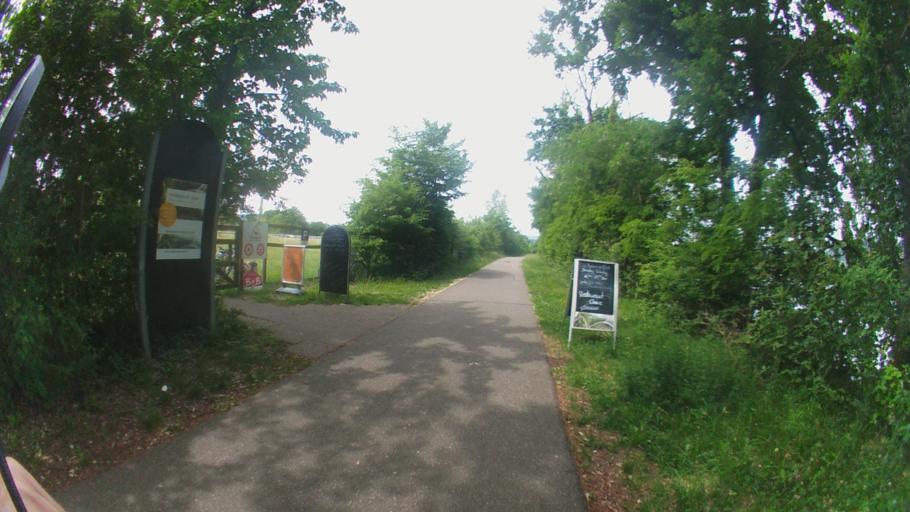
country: CH
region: Aargau
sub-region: Bezirk Zurzach
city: Klingnau
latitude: 47.5782
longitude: 8.2376
